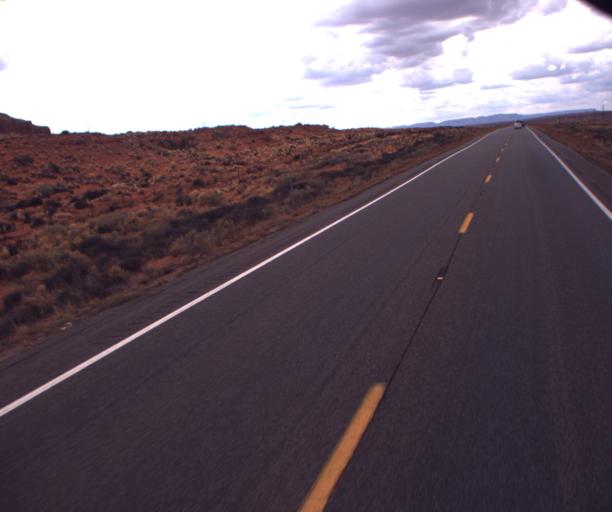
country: US
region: Arizona
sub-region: Navajo County
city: Kayenta
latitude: 36.7970
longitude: -109.9338
